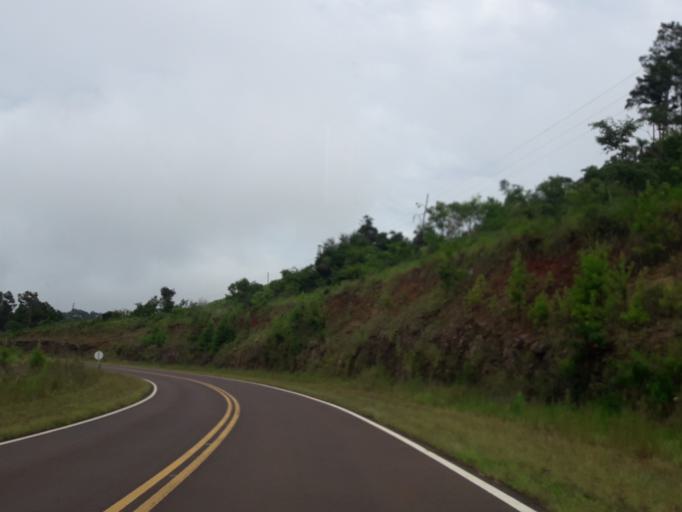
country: AR
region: Misiones
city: Bernardo de Irigoyen
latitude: -26.3958
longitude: -53.8138
